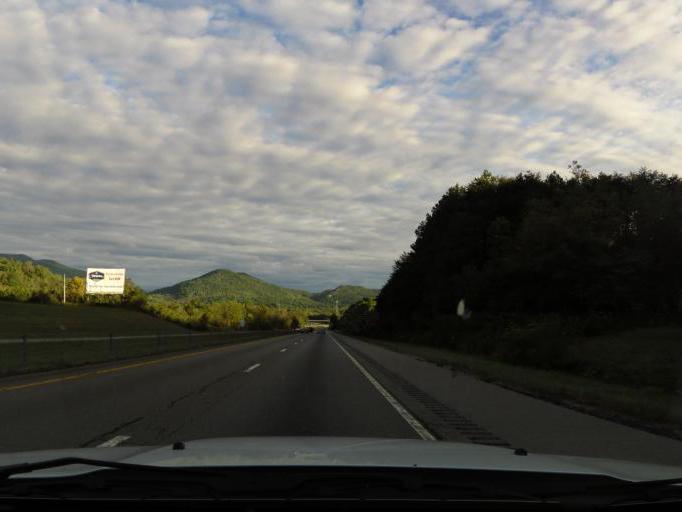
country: US
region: Tennessee
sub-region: Campbell County
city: Caryville
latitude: 36.2898
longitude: -84.2139
